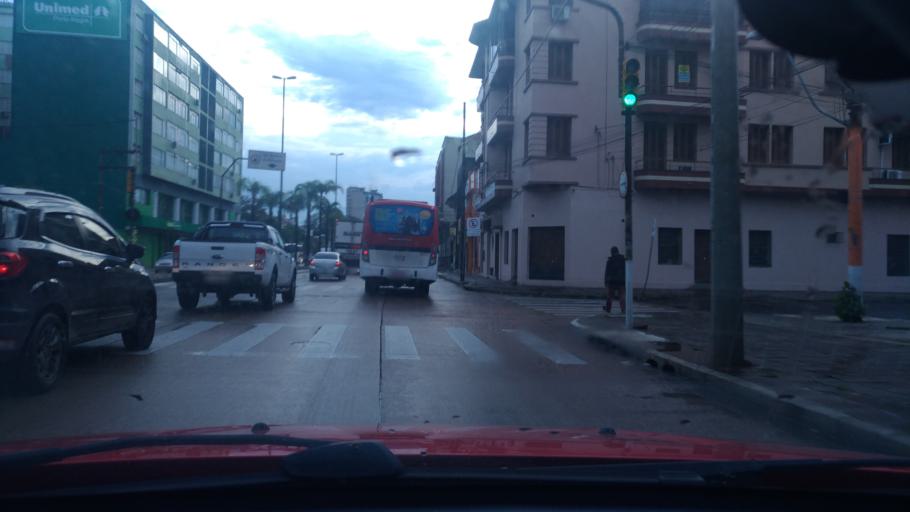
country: BR
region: Rio Grande do Sul
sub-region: Porto Alegre
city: Porto Alegre
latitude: -30.0176
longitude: -51.2085
